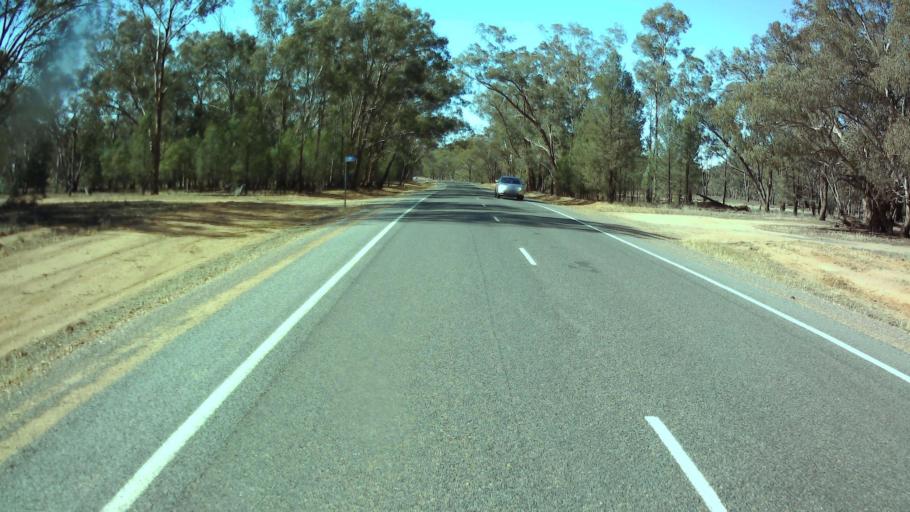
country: AU
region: New South Wales
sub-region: Weddin
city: Grenfell
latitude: -33.7606
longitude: 148.0823
